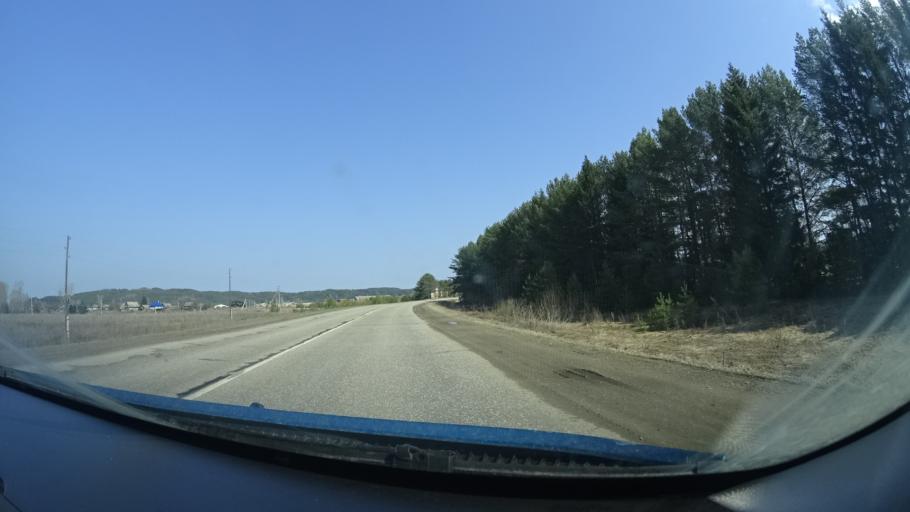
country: RU
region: Perm
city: Osa
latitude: 57.2888
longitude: 55.5750
